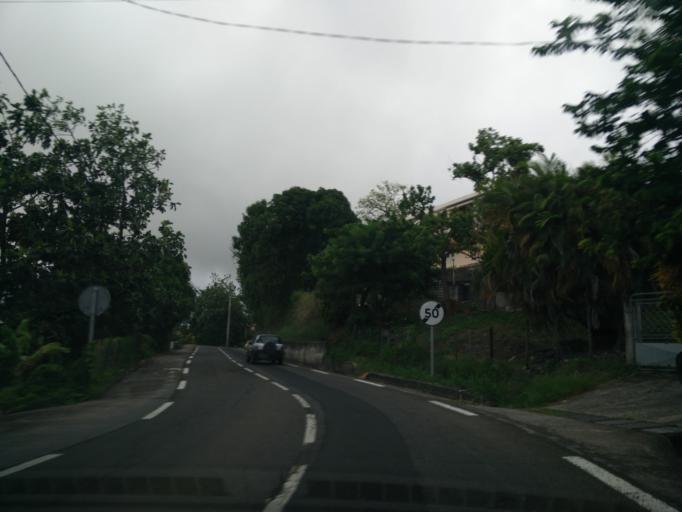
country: MQ
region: Martinique
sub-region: Martinique
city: Le Marin
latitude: 14.4921
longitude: -60.8601
